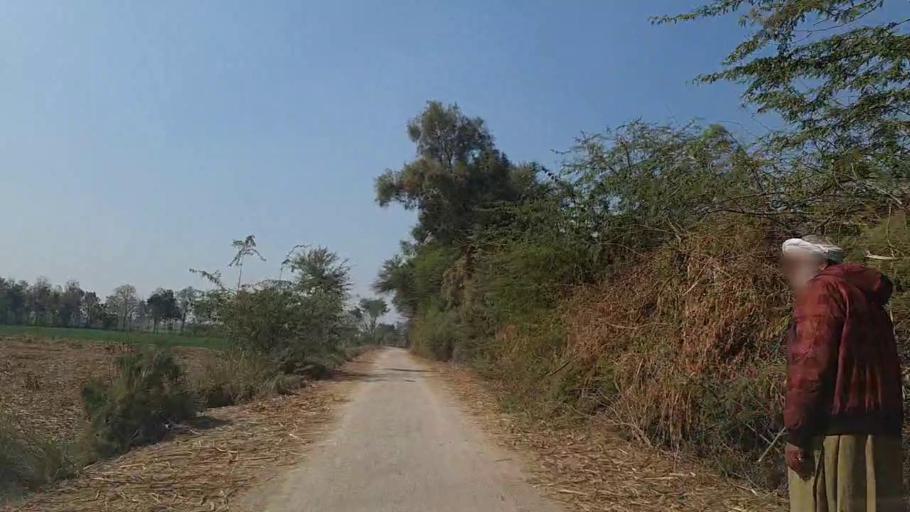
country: PK
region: Sindh
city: Daur
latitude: 26.5032
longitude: 68.3248
